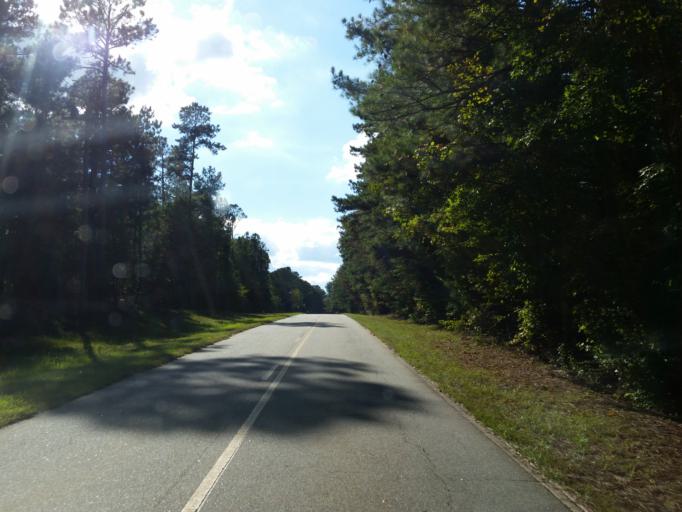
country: US
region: Georgia
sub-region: Butts County
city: Indian Springs
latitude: 33.2024
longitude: -83.9972
